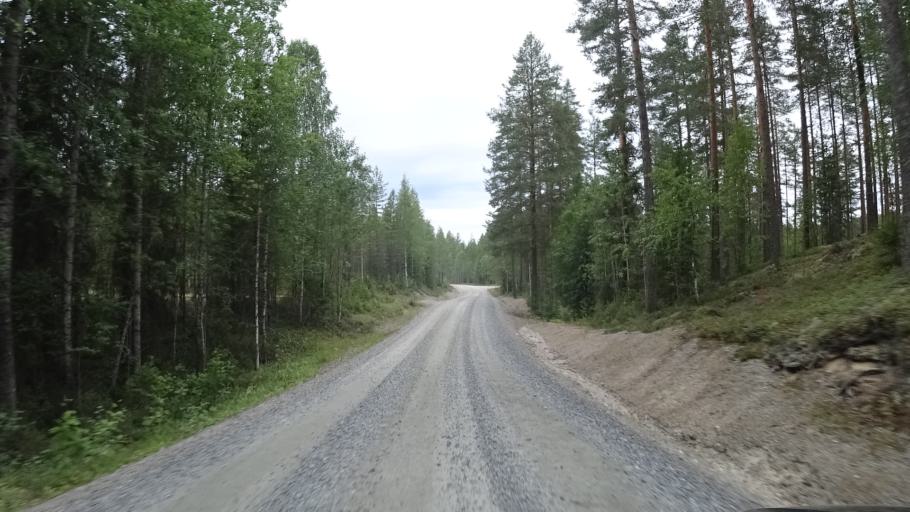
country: FI
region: North Karelia
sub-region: Pielisen Karjala
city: Lieksa
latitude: 63.2396
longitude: 30.3508
